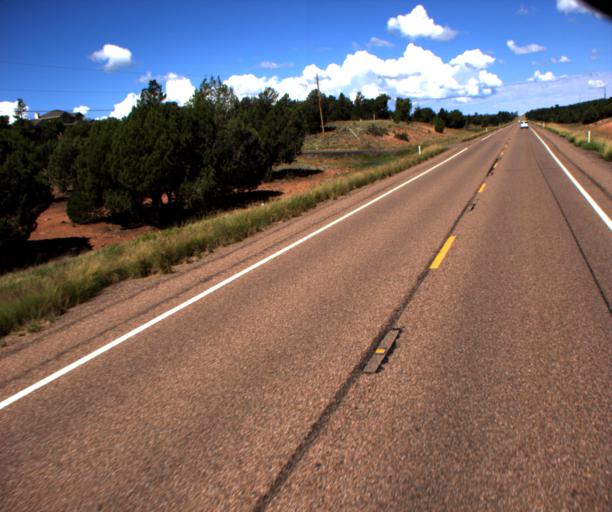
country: US
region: Arizona
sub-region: Navajo County
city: Linden
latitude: 34.3225
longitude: -110.2536
